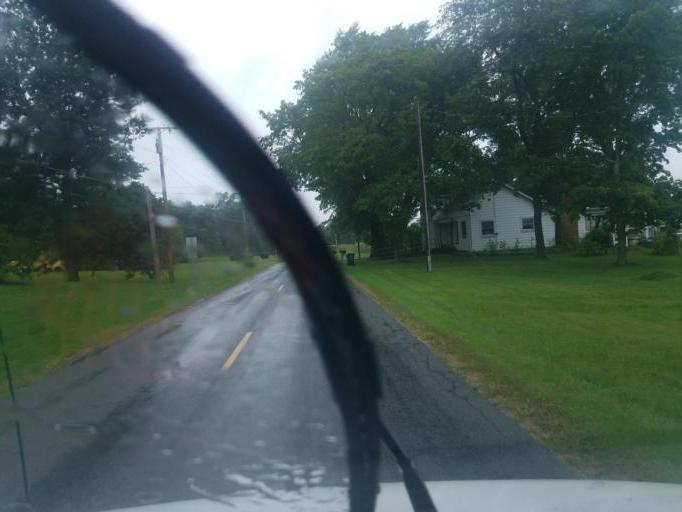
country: US
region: Ohio
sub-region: Medina County
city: Seville
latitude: 41.0241
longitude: -81.8325
